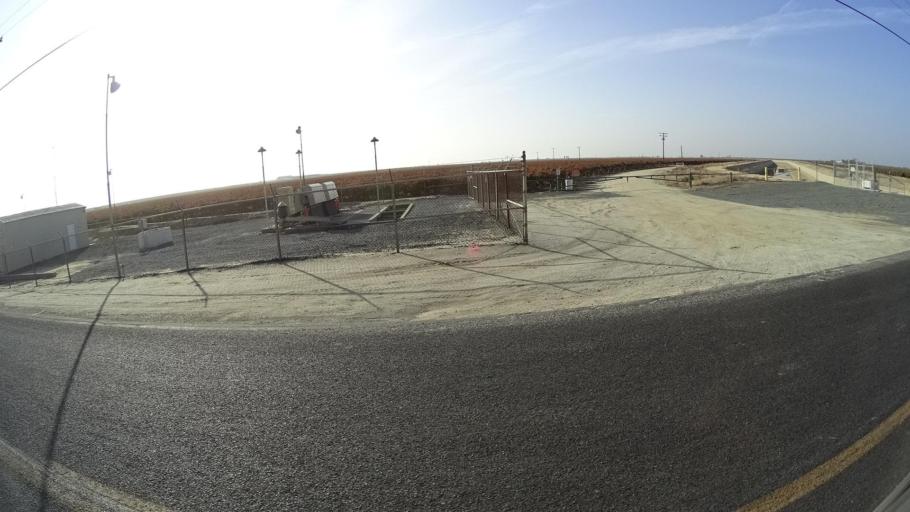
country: US
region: California
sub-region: Kern County
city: McFarland
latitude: 35.6746
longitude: -119.1950
